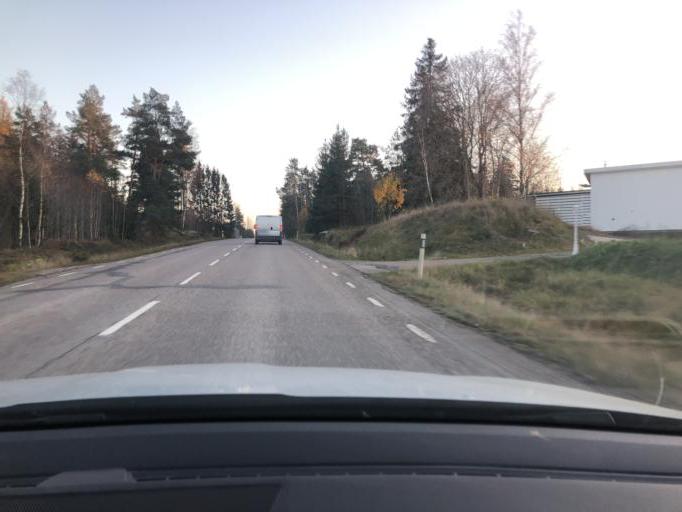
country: SE
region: Soedermanland
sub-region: Strangnas Kommun
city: Akers Styckebruk
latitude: 59.3019
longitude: 17.0976
